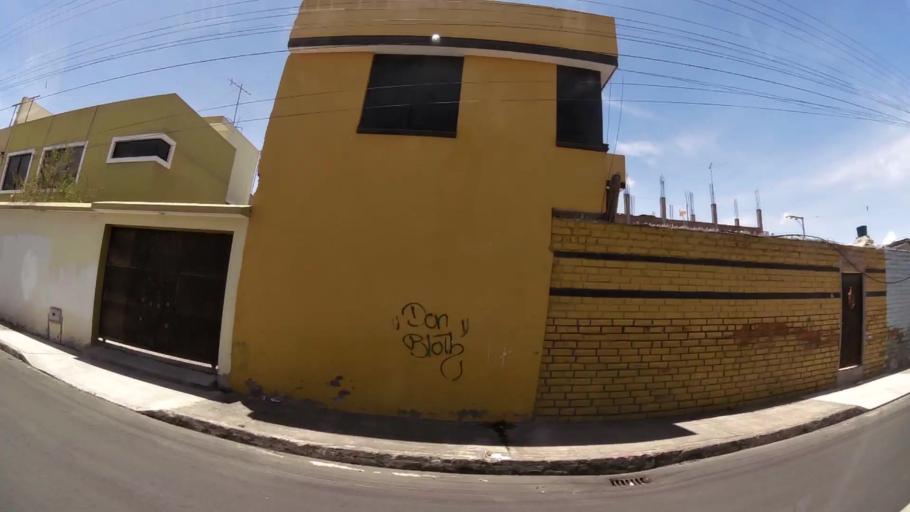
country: EC
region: Chimborazo
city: Riobamba
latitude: -1.6762
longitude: -78.6382
